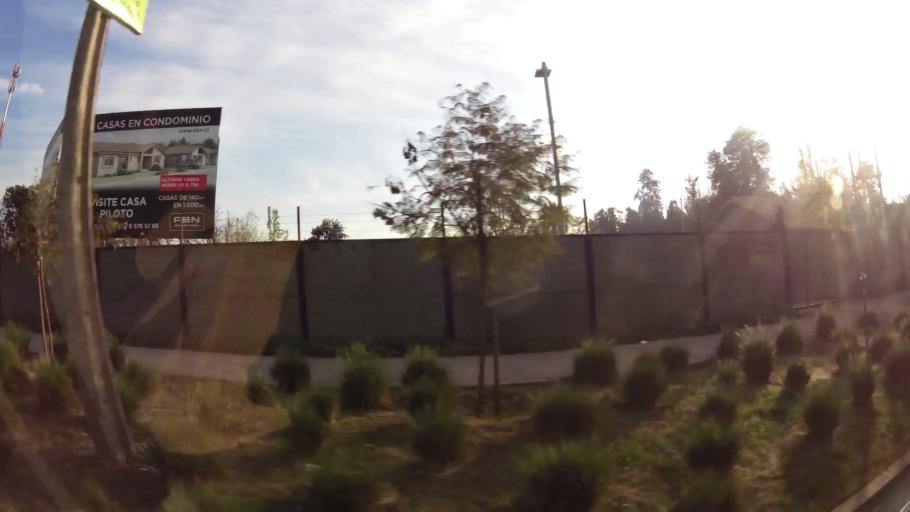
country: CL
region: Santiago Metropolitan
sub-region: Provincia de Maipo
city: San Bernardo
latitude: -33.5600
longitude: -70.7673
